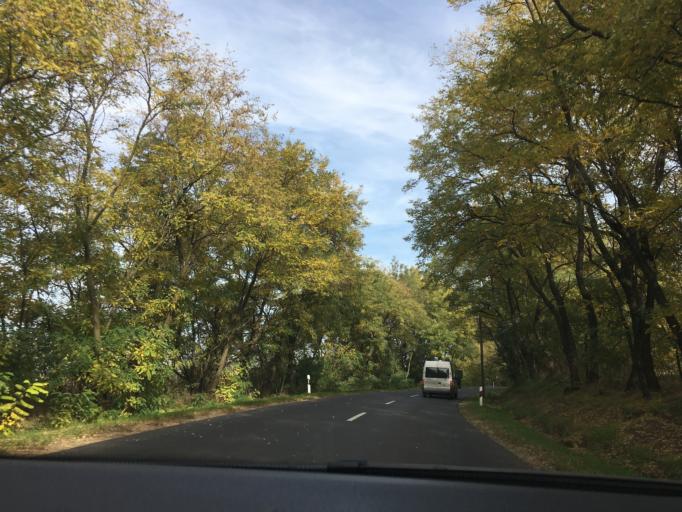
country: HU
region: Szabolcs-Szatmar-Bereg
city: Nagykallo
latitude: 47.8536
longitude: 21.7943
